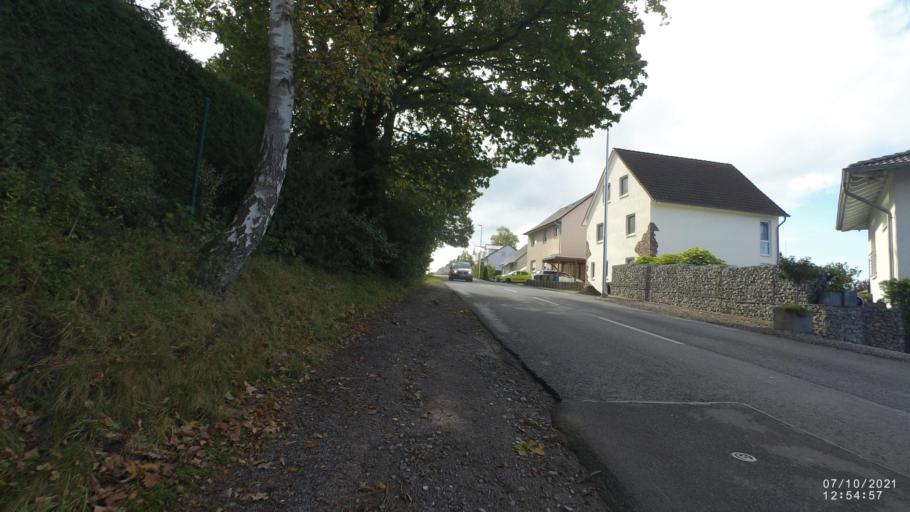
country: DE
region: North Rhine-Westphalia
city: Iserlohn
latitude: 51.4083
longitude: 7.7173
